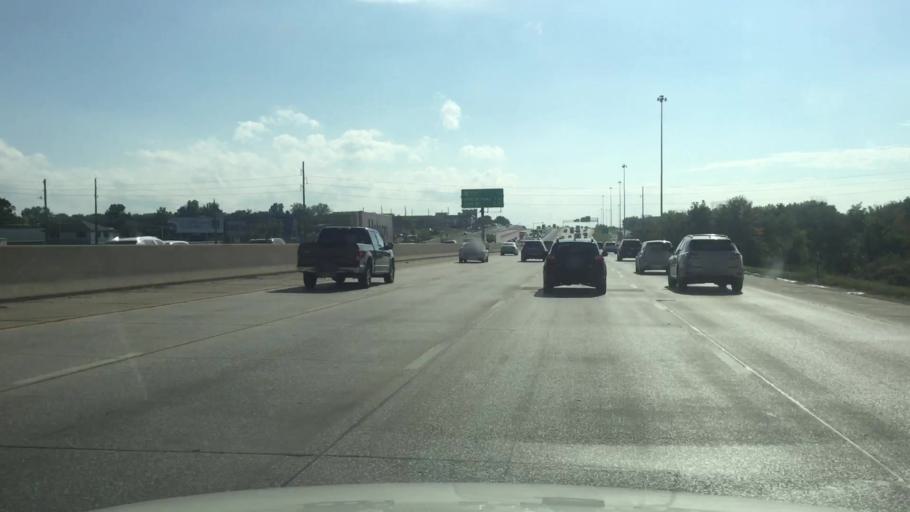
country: US
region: Kansas
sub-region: Johnson County
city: Overland Park
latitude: 38.9889
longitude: -94.7021
